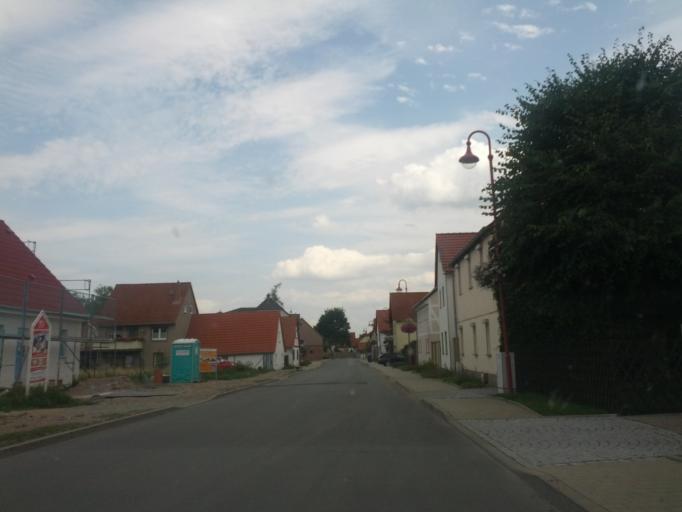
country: DE
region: Thuringia
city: Ichtershausen
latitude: 50.8866
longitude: 10.9420
